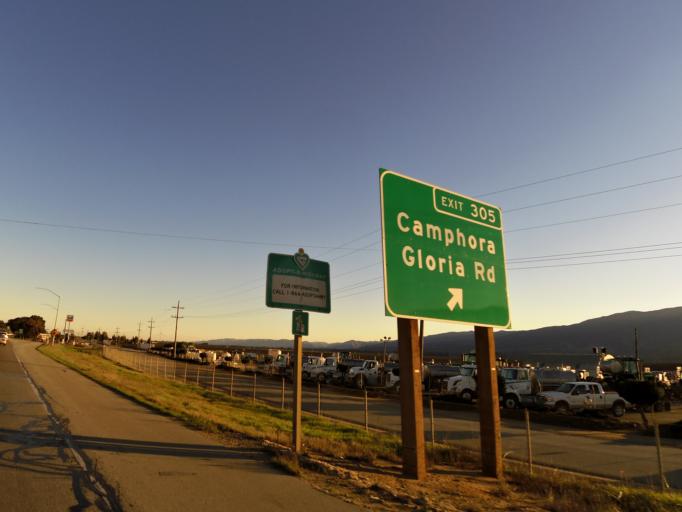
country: US
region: California
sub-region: Monterey County
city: Soledad
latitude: 36.4523
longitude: -121.3682
